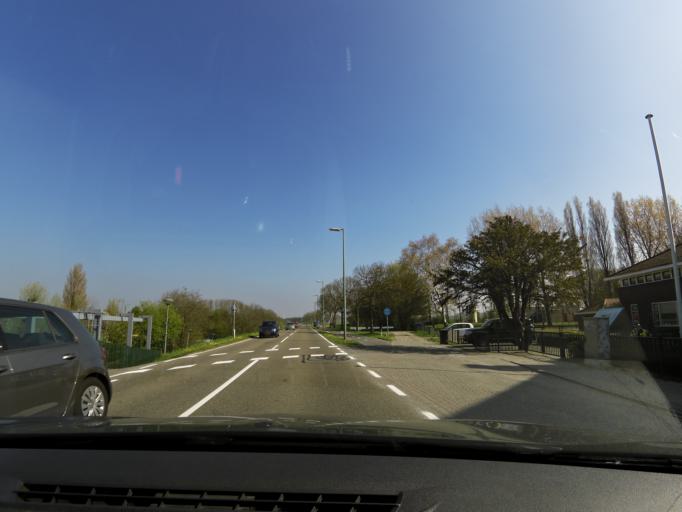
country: NL
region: South Holland
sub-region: Gemeente Maassluis
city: Maassluis
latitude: 51.9144
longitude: 4.2589
